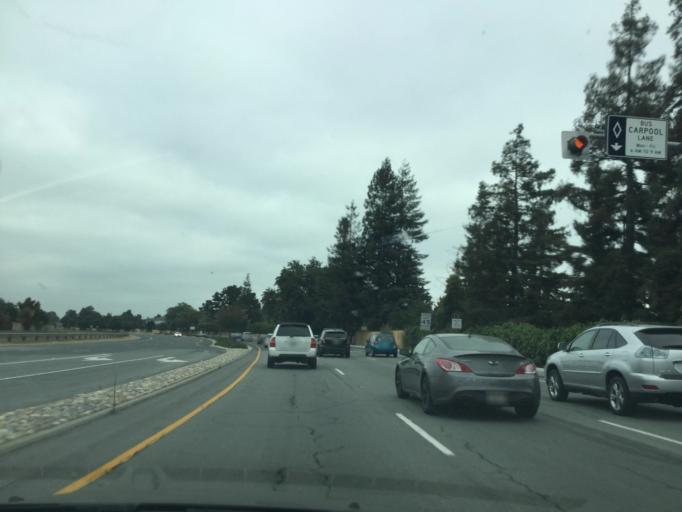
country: US
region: California
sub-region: Santa Clara County
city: Campbell
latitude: 37.2951
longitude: -121.9607
